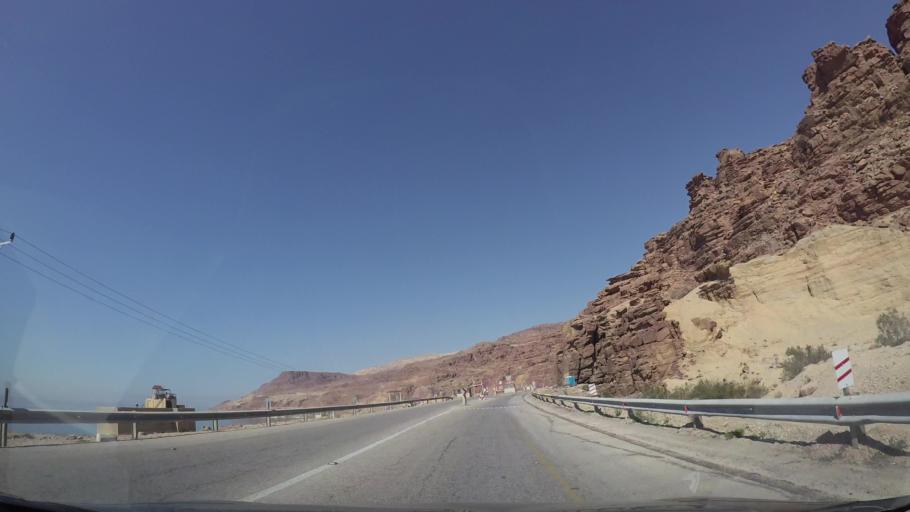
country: JO
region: Karak
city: Al Qasr
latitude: 31.4688
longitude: 35.5730
